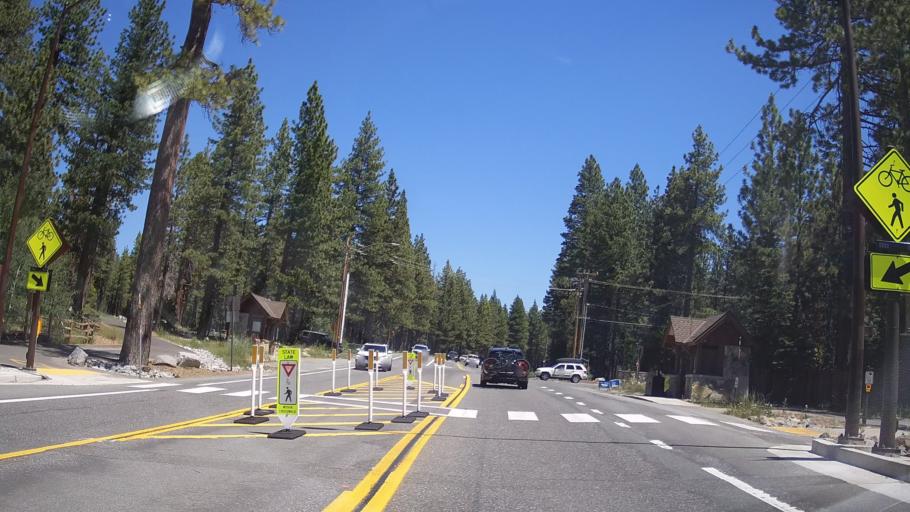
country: US
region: California
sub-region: Placer County
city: Dollar Point
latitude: 39.1919
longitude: -120.1052
